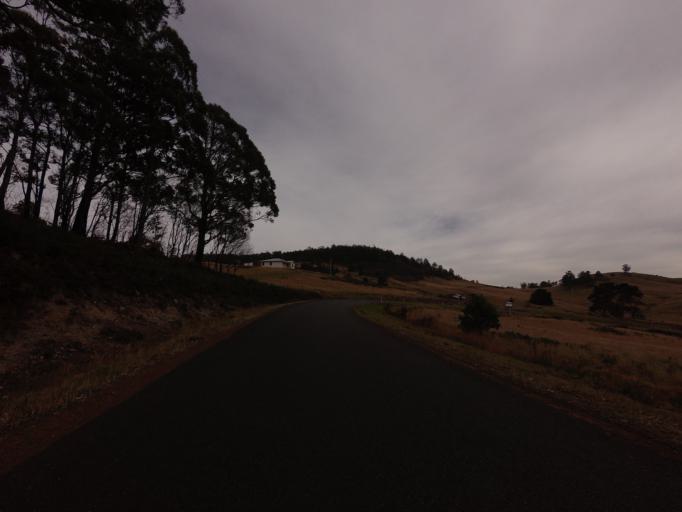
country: AU
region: Tasmania
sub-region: Sorell
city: Sorell
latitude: -42.4881
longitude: 147.5645
